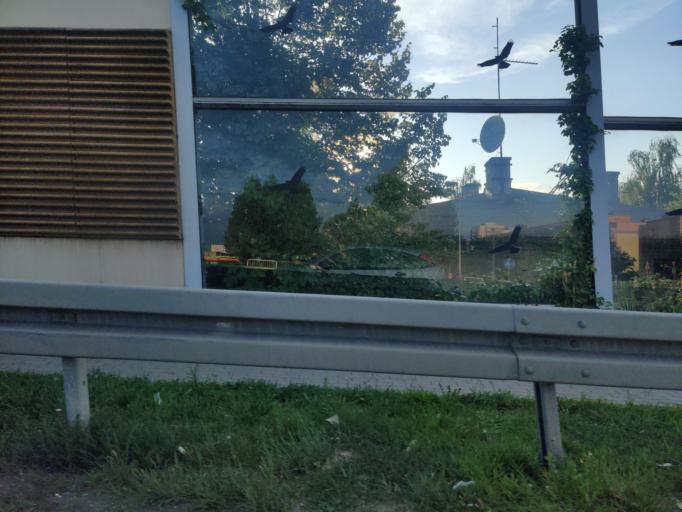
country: PL
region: Greater Poland Voivodeship
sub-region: Konin
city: Konin
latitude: 52.2340
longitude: 18.2461
